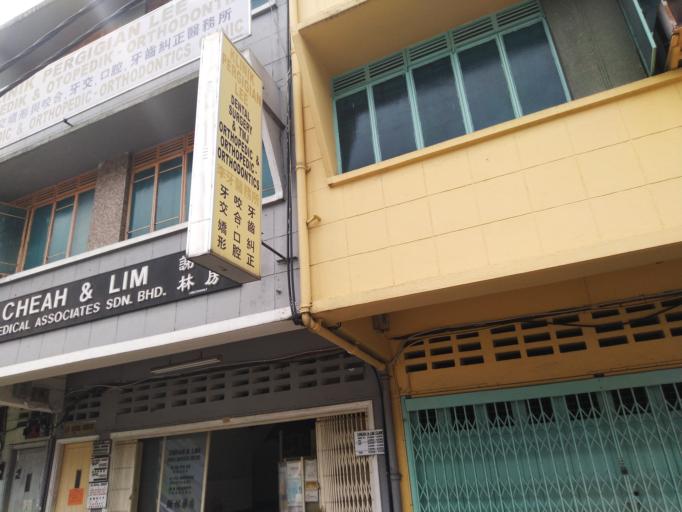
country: MY
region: Perak
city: Ipoh
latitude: 4.5999
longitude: 101.0856
